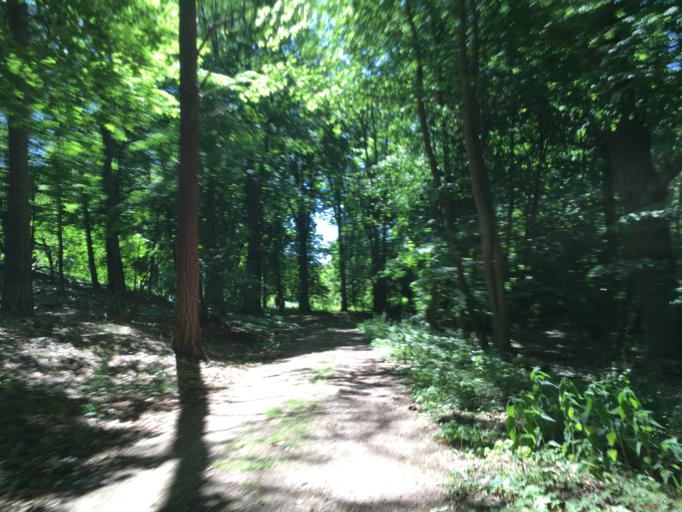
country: DE
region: Brandenburg
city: Zehdenick
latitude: 52.9048
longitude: 13.2415
